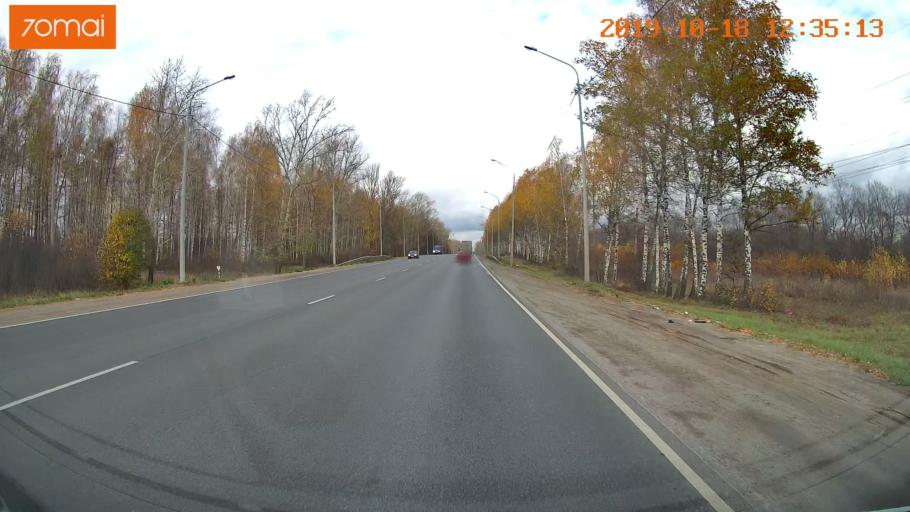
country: RU
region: Rjazan
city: Ryazan'
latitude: 54.6221
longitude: 39.6361
